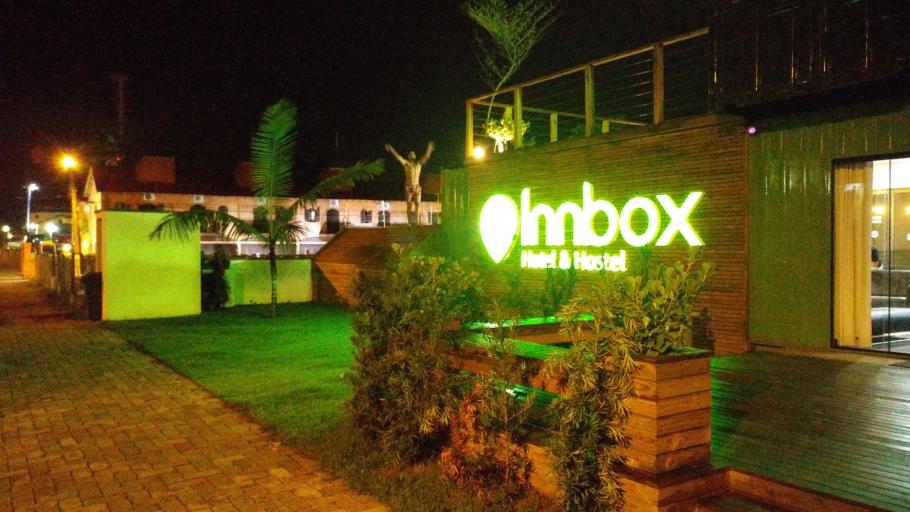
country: BR
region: Santa Catarina
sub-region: Florianopolis
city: Itacorubi
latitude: -27.4321
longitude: -48.4604
